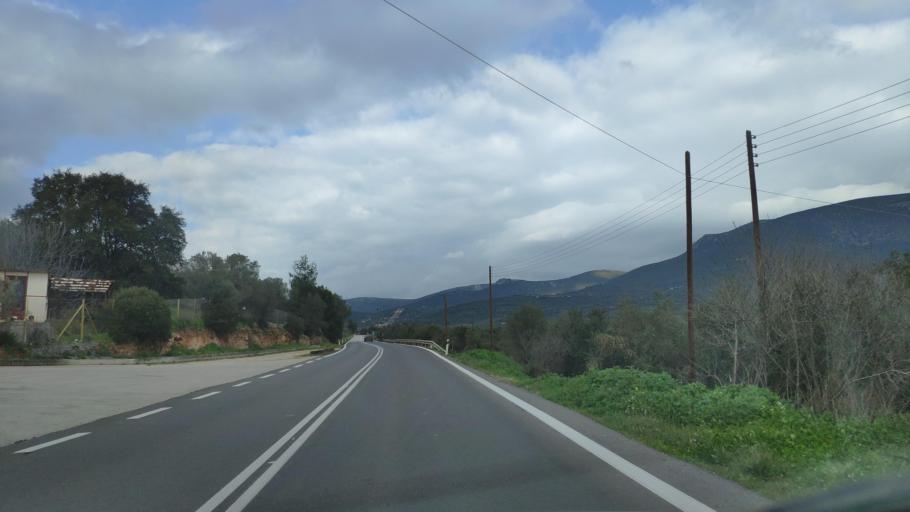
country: GR
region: Peloponnese
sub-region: Nomos Argolidos
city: Koutsopodi
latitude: 37.7444
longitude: 22.7346
